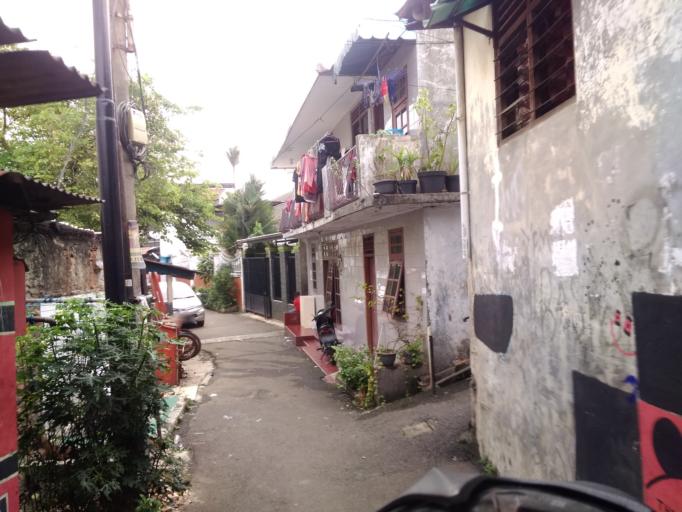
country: ID
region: Jakarta Raya
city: Jakarta
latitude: -6.2618
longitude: 106.7916
